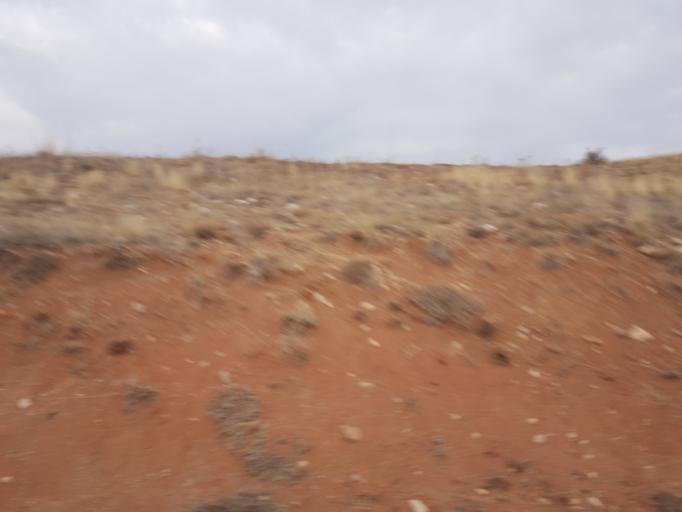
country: TR
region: Corum
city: Cemilbey
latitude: 40.2458
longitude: 35.0665
